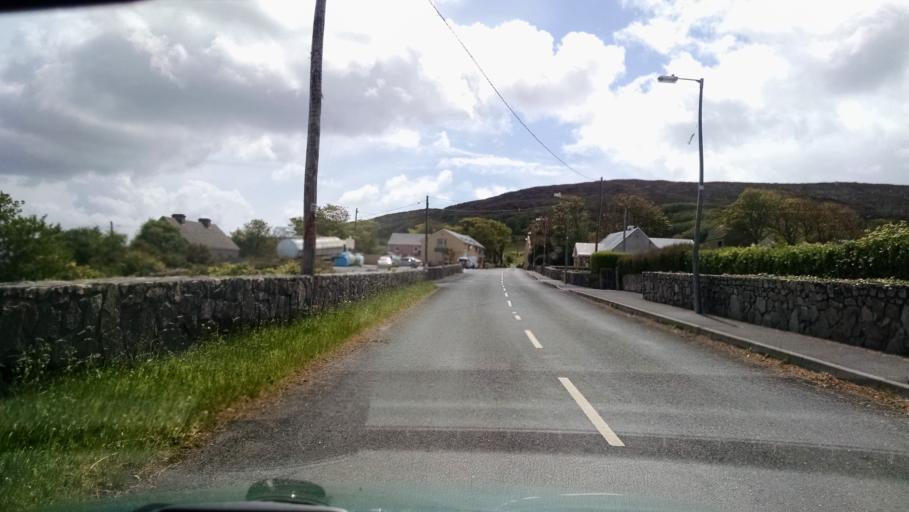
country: IE
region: Connaught
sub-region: County Galway
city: Clifden
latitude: 53.3243
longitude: -9.7362
